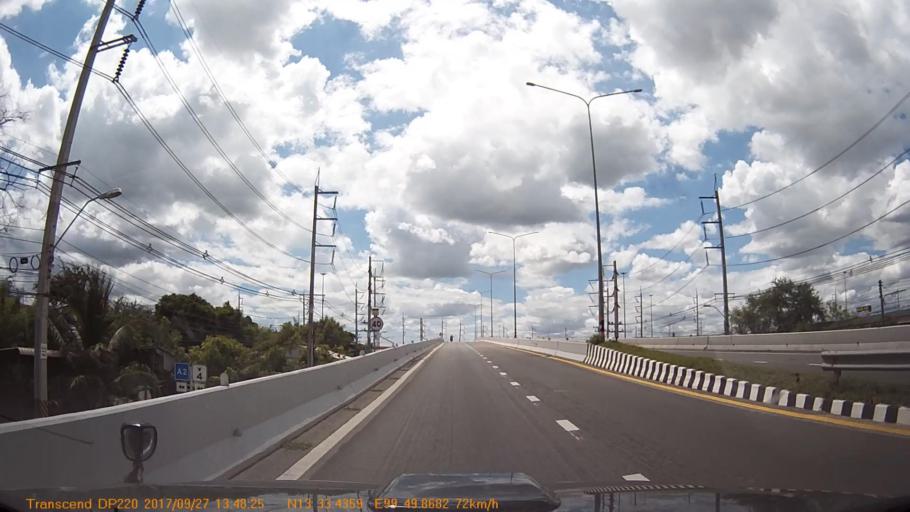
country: TH
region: Ratchaburi
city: Ratchaburi
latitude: 13.5573
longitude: 99.8312
